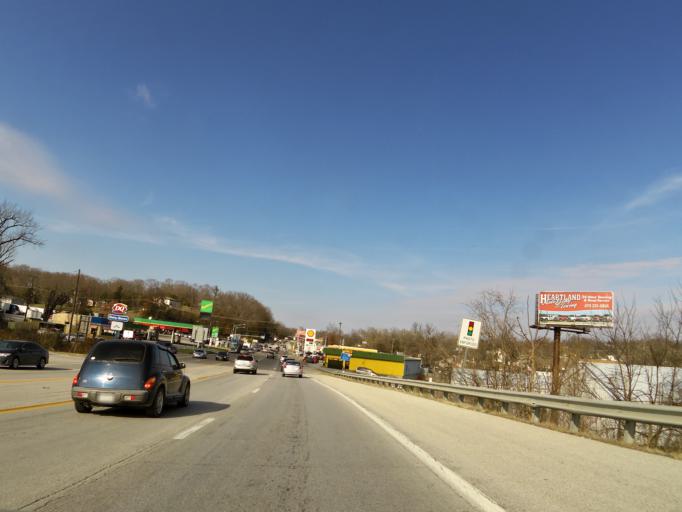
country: US
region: Missouri
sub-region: Marion County
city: Hannibal
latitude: 39.7041
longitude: -91.3879
